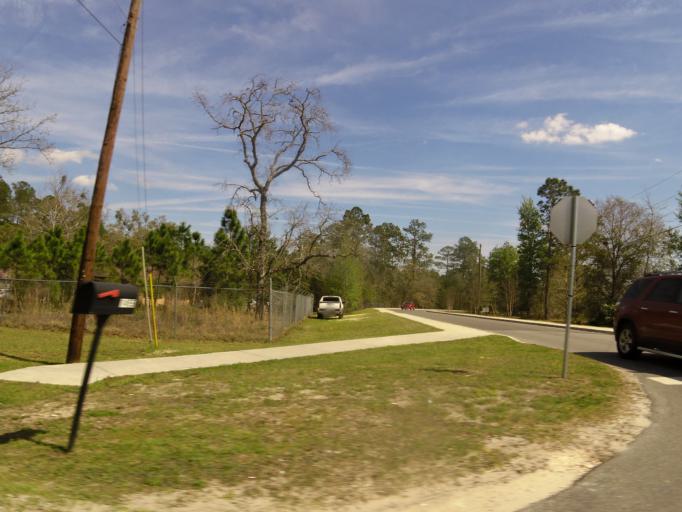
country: US
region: Florida
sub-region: Clay County
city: Middleburg
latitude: 30.1043
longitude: -81.8645
